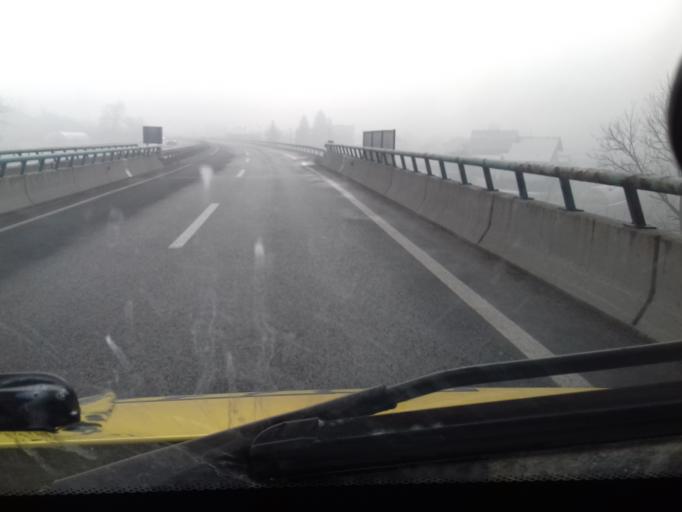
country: BA
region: Federation of Bosnia and Herzegovina
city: Ilijas
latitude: 43.9491
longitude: 18.2549
